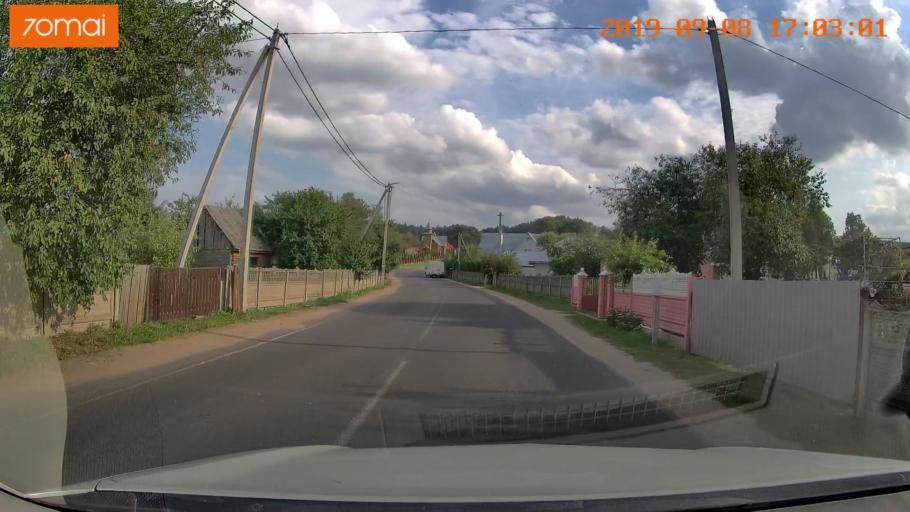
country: BY
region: Grodnenskaya
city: Hrodna
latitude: 53.6982
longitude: 23.9414
